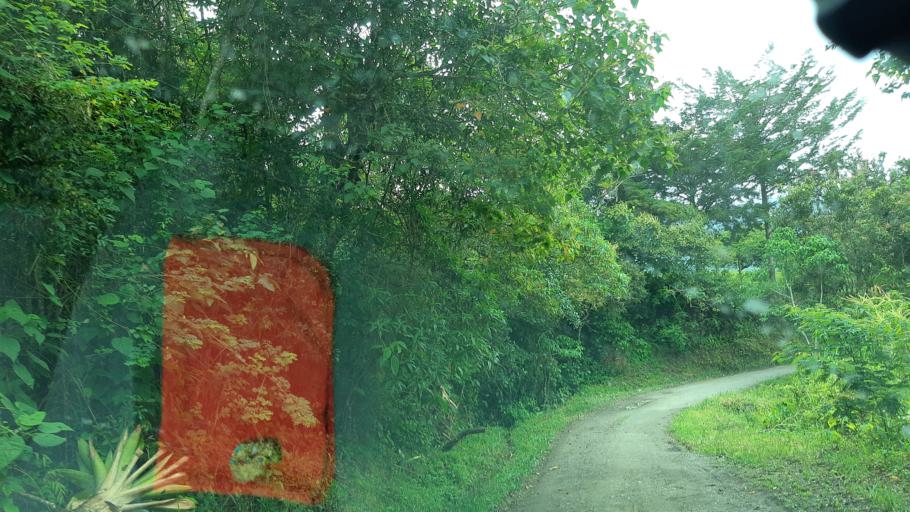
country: CO
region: Boyaca
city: Garagoa
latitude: 5.0372
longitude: -73.3562
